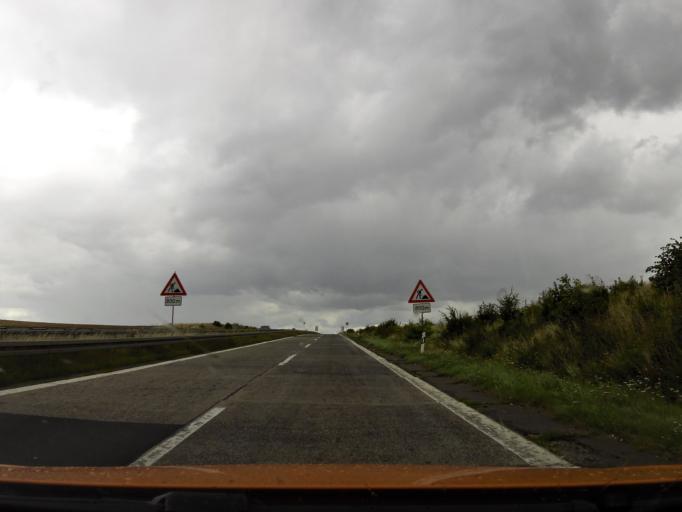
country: DE
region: Brandenburg
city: Gramzow
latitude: 53.2856
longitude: 14.0862
